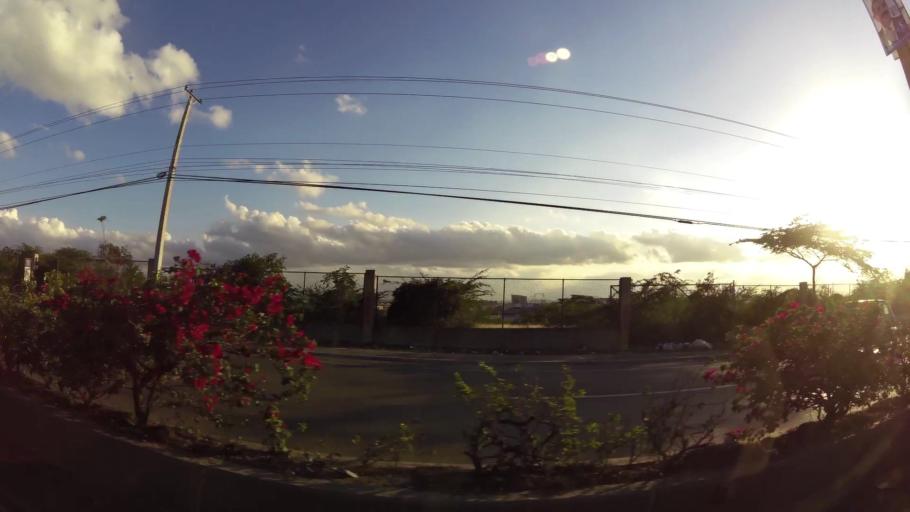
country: DO
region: Santiago
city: Palmar Arriba
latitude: 19.4936
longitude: -70.7299
